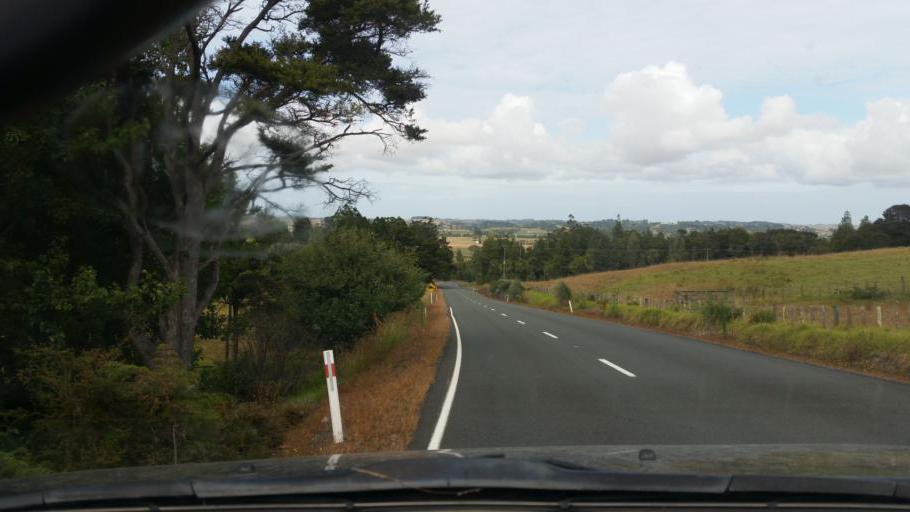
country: NZ
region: Northland
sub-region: Kaipara District
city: Dargaville
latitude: -35.9486
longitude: 173.9041
